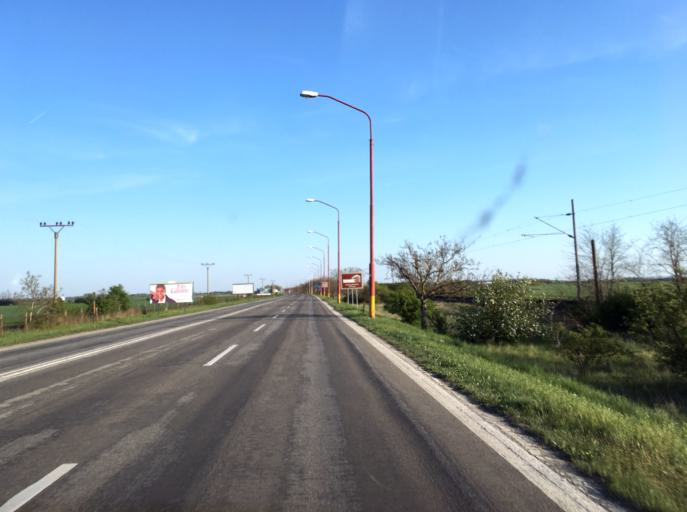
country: HU
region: Gyor-Moson-Sopron
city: Rajka
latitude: 48.0285
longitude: 17.1686
